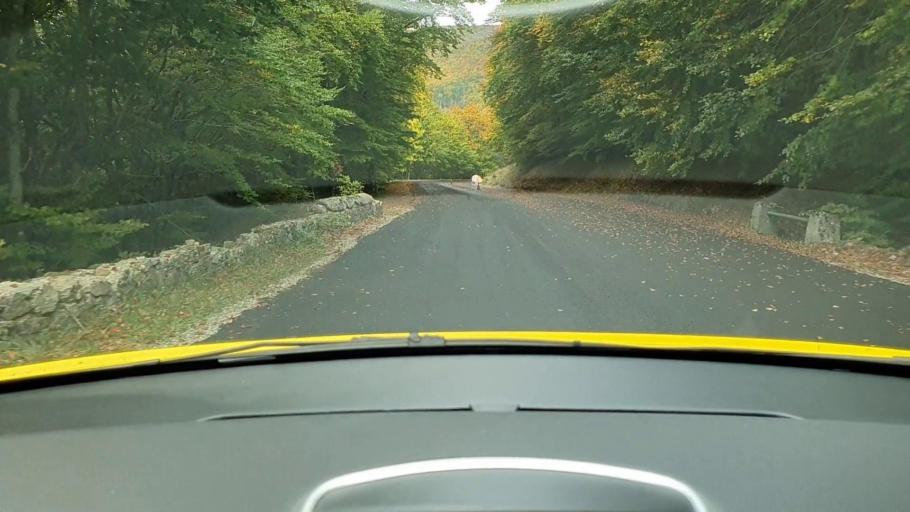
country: FR
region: Languedoc-Roussillon
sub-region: Departement du Gard
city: Valleraugue
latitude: 44.0770
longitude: 3.5325
